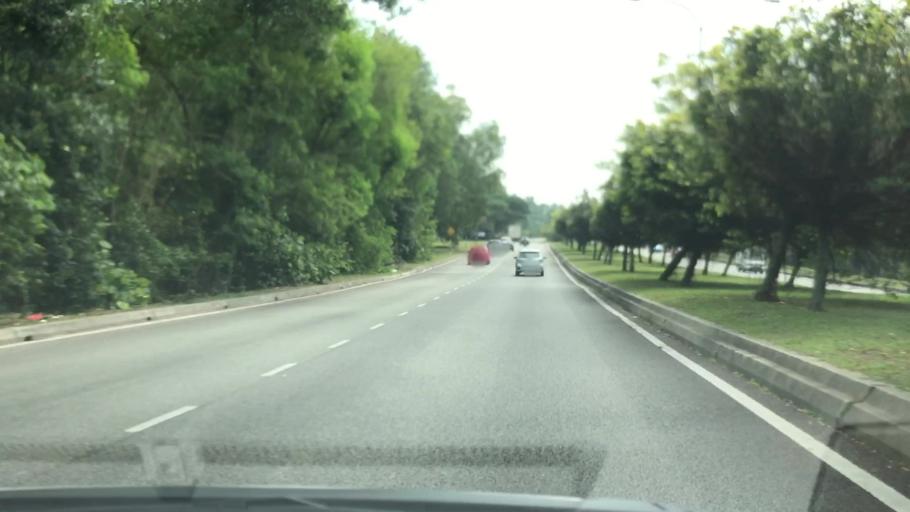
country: MY
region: Putrajaya
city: Putrajaya
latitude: 3.0035
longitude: 101.6653
